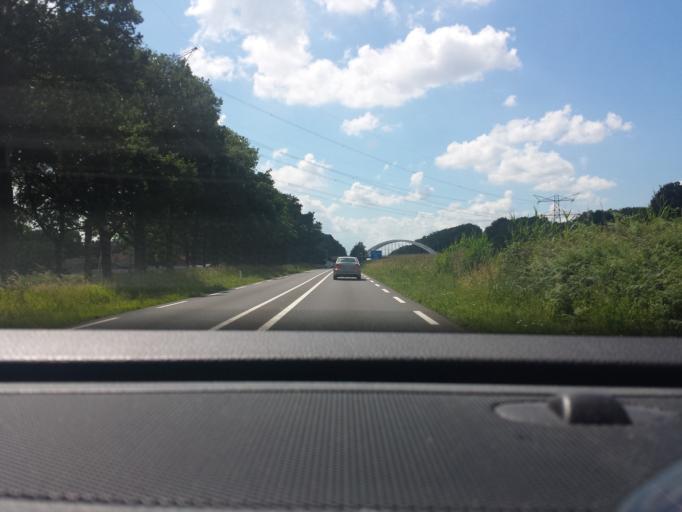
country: NL
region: Overijssel
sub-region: Gemeente Hof van Twente
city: Goor
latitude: 52.2243
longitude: 6.5858
